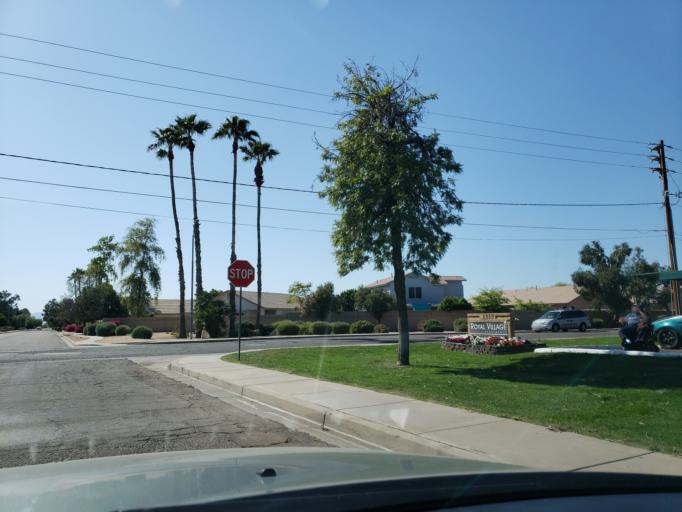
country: US
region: Arizona
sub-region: Maricopa County
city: Glendale
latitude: 33.5567
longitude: -112.1903
